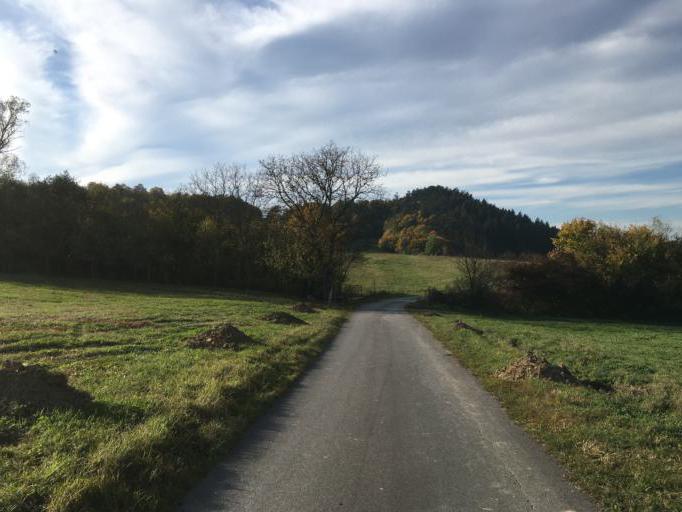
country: SK
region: Trenciansky
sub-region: Okres Povazska Bystrica
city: Povazska Bystrica
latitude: 49.0551
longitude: 18.3979
